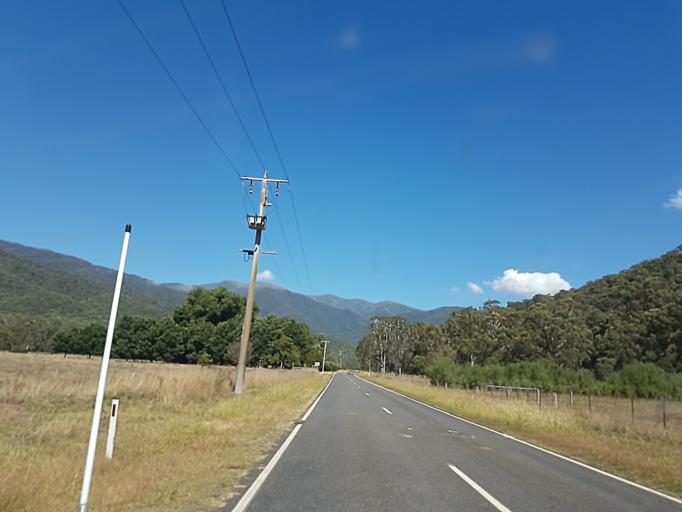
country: AU
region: Victoria
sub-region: Alpine
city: Mount Beauty
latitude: -36.8298
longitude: 147.0721
